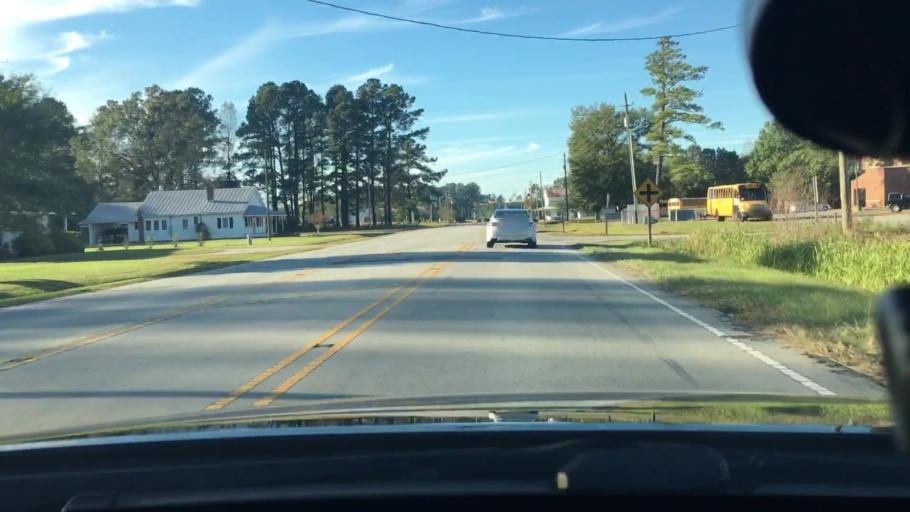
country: US
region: North Carolina
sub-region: Pitt County
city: Windsor
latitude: 35.4624
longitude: -77.2731
